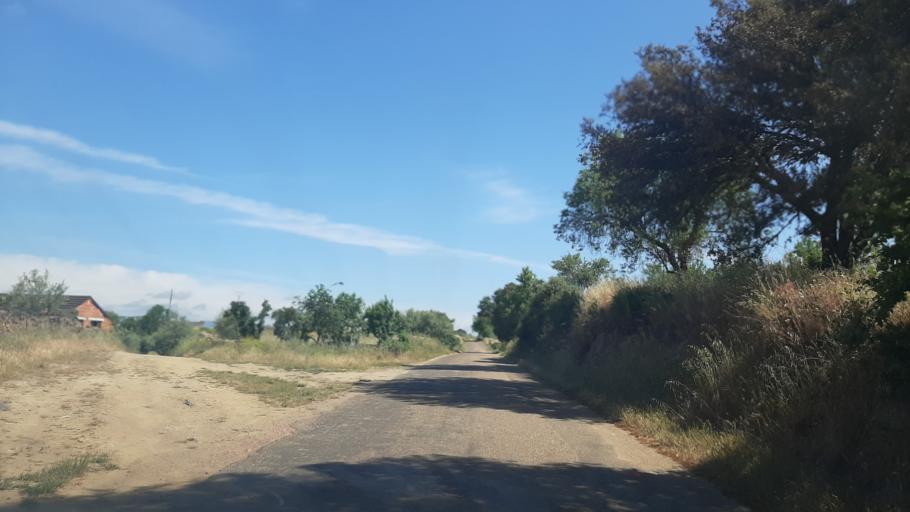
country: ES
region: Castille and Leon
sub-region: Provincia de Salamanca
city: Zamarra
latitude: 40.5187
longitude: -6.4500
